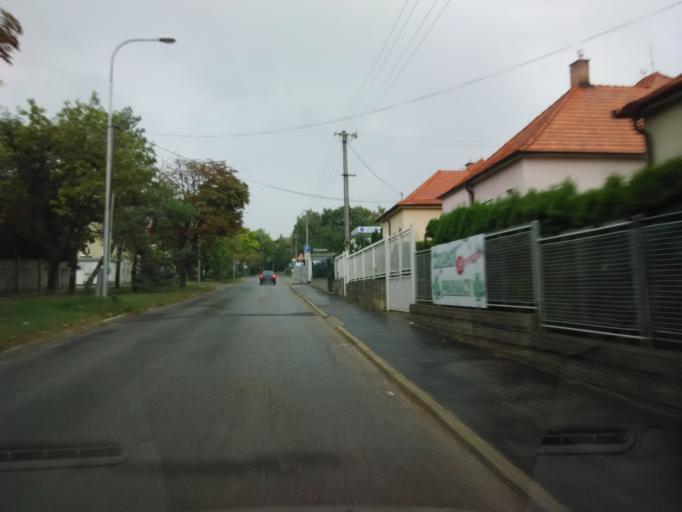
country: SK
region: Nitriansky
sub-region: Okres Nitra
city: Nitra
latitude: 48.2987
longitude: 18.0831
